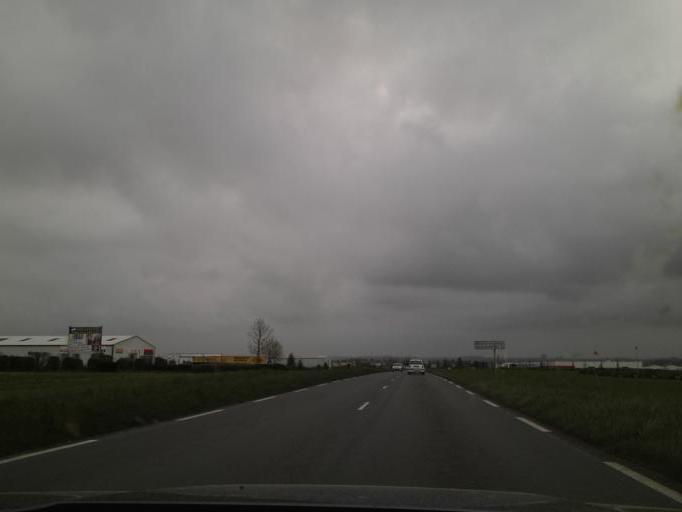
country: FR
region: Pays de la Loire
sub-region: Departement de la Vendee
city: Fontenay-le-Comte
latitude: 46.4427
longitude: -0.8183
